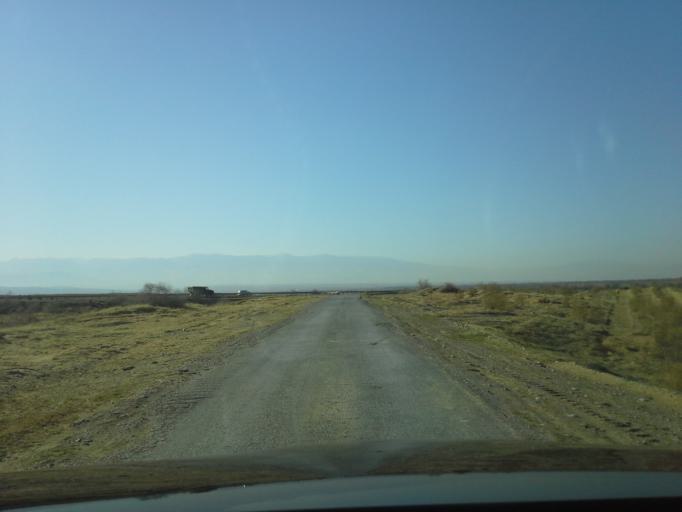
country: TM
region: Ahal
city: Annau
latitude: 37.8926
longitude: 58.6133
